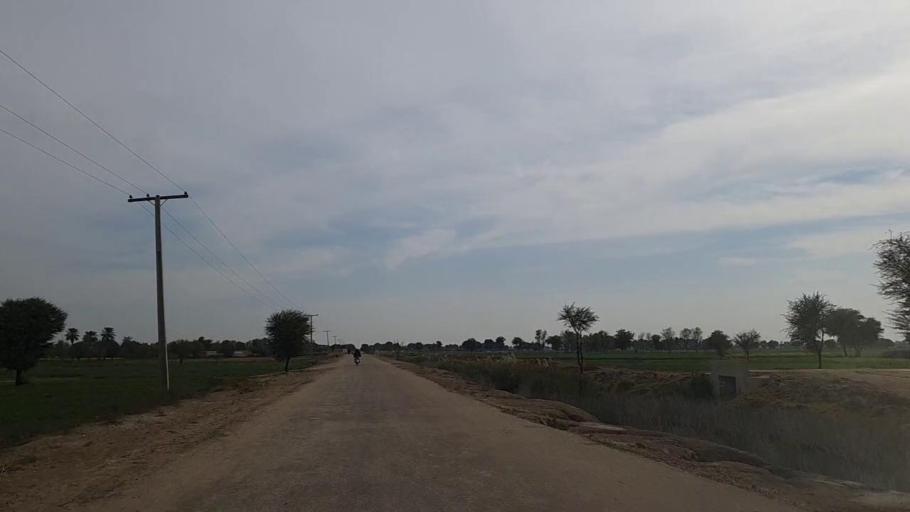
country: PK
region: Sindh
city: Daur
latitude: 26.4222
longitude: 68.4853
